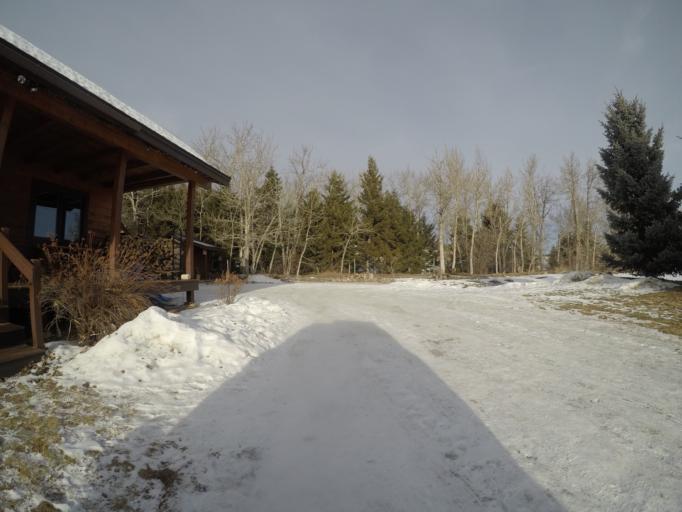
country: US
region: Montana
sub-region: Carbon County
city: Red Lodge
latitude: 45.1593
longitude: -109.2995
